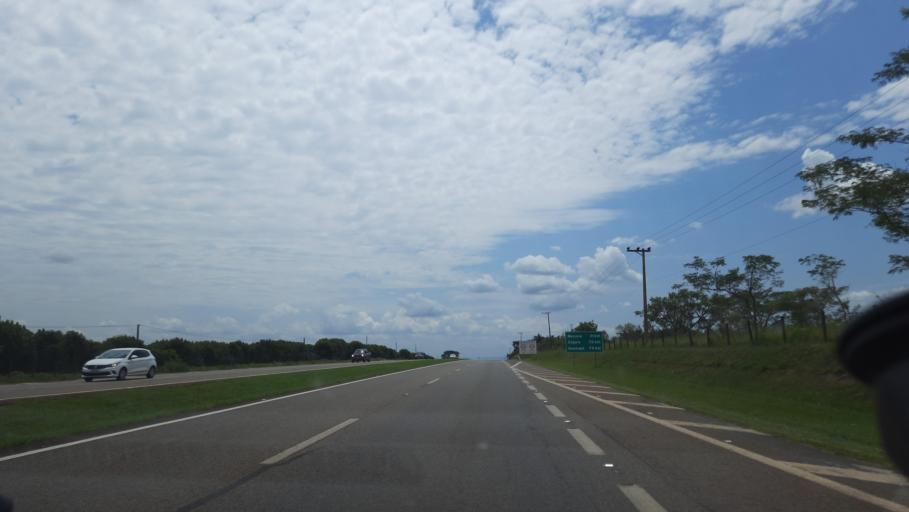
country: BR
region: Sao Paulo
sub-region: Casa Branca
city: Casa Branca
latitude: -21.7463
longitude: -47.0722
